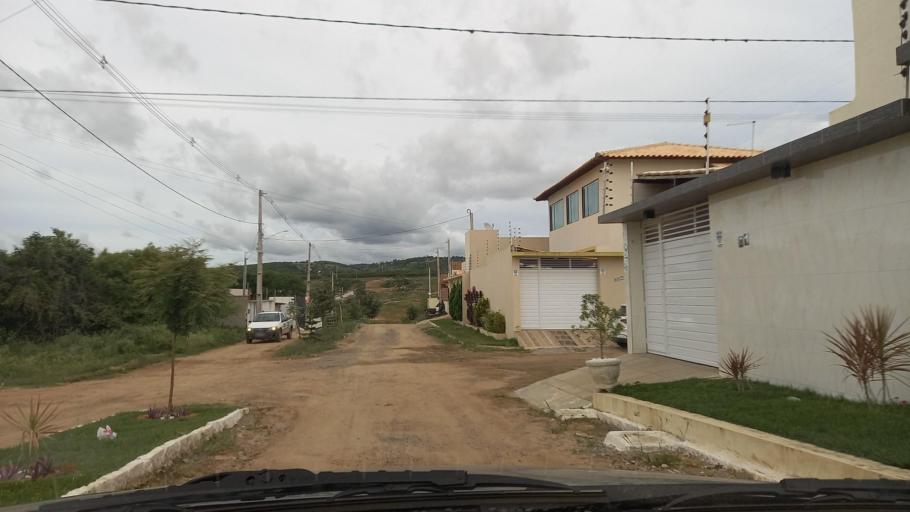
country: BR
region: Pernambuco
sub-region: Gravata
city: Gravata
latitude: -8.2232
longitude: -35.5744
